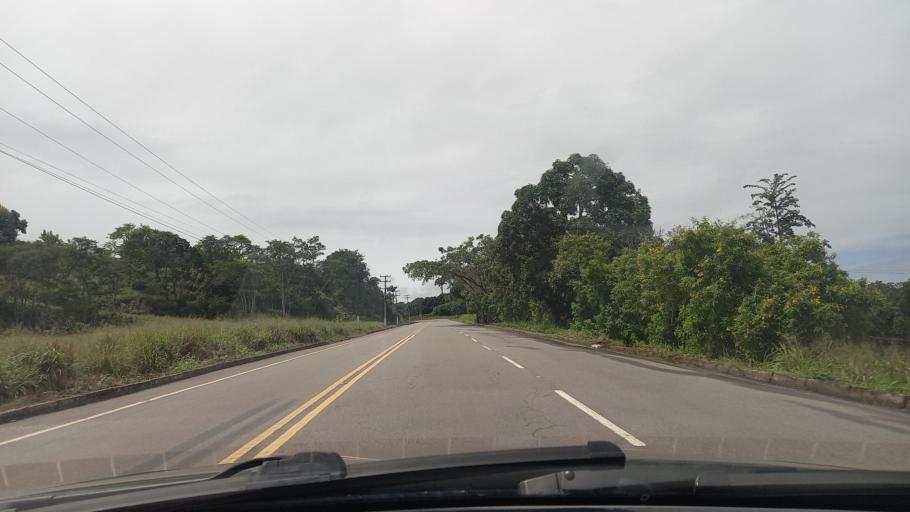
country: BR
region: Alagoas
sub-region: Sao Miguel Dos Campos
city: Sao Miguel dos Campos
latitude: -9.8090
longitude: -36.2154
